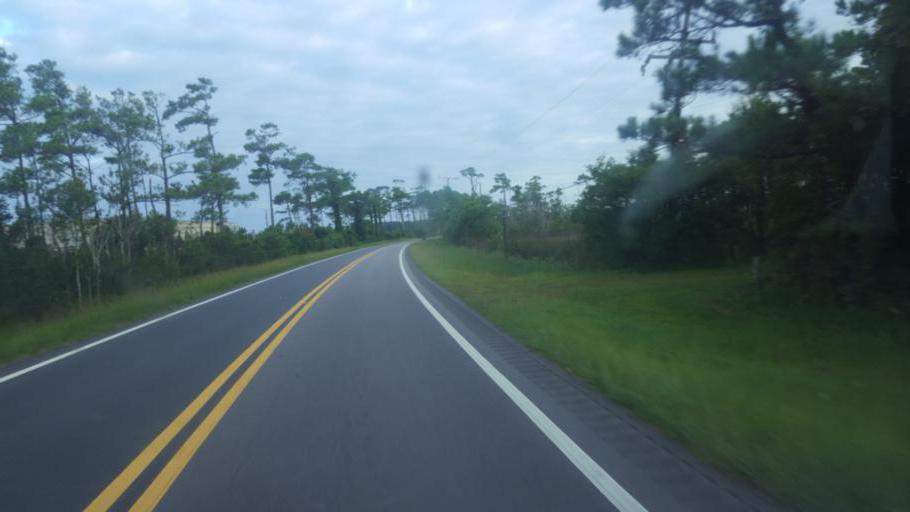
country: US
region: North Carolina
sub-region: Dare County
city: Wanchese
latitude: 35.8707
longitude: -75.6527
